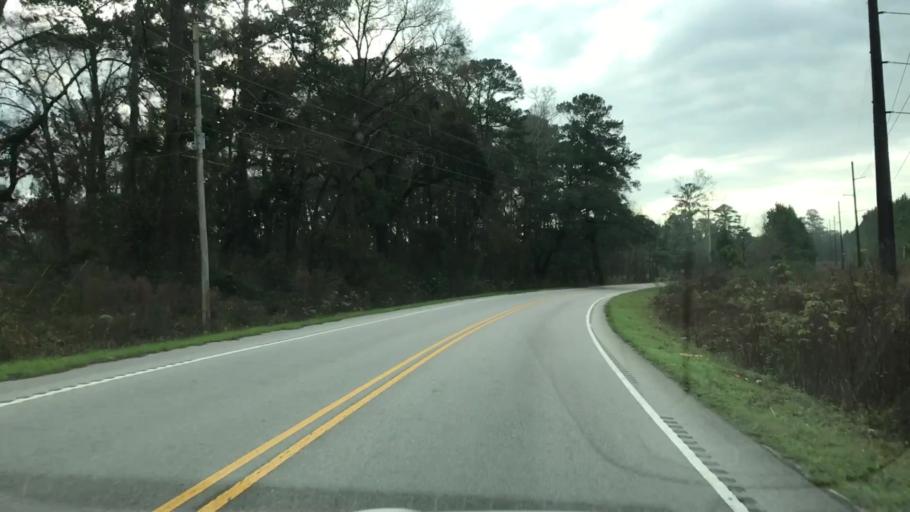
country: US
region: South Carolina
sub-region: Jasper County
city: Ridgeland
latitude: 32.5214
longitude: -80.8913
